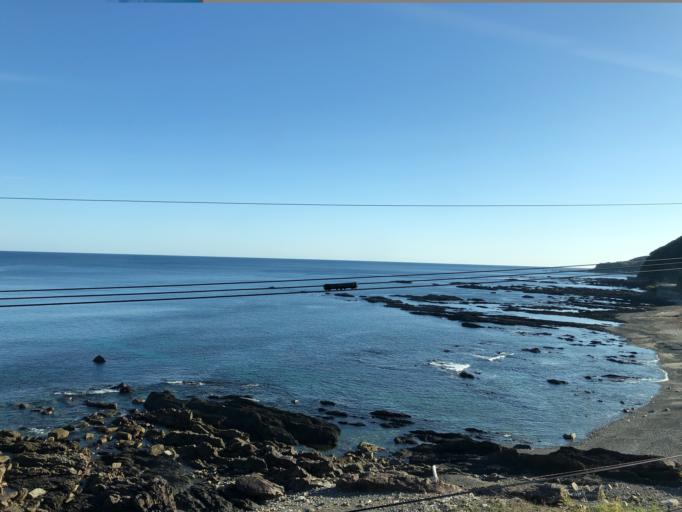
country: JP
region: Kochi
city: Nakamura
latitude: 33.0503
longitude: 133.0965
